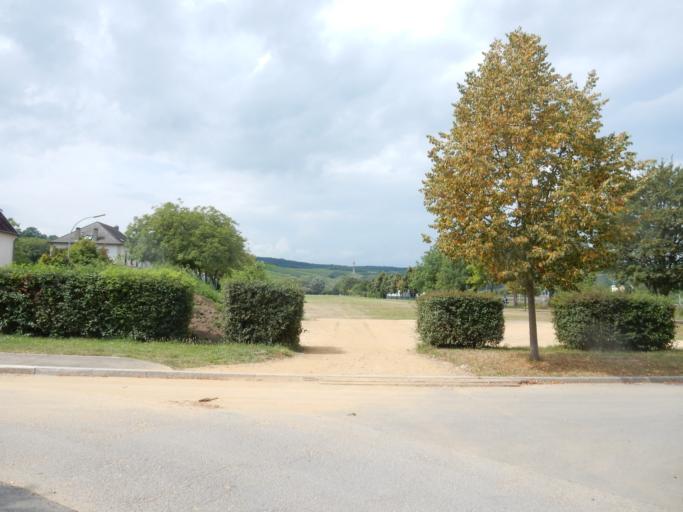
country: DE
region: Rheinland-Pfalz
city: Palzem
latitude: 49.5648
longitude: 6.3680
